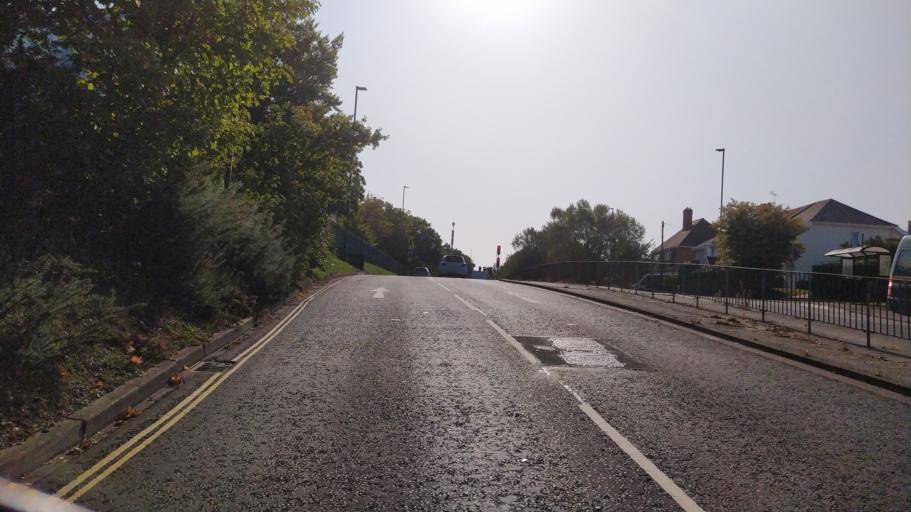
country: GB
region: England
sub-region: Hampshire
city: West End
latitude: 50.9042
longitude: -1.3371
